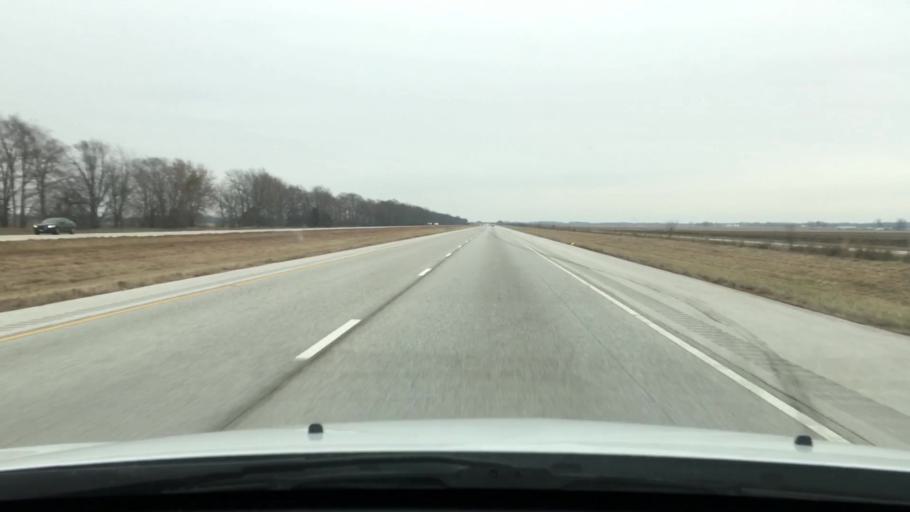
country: US
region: Illinois
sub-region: Scott County
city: Winchester
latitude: 39.6801
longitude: -90.3730
